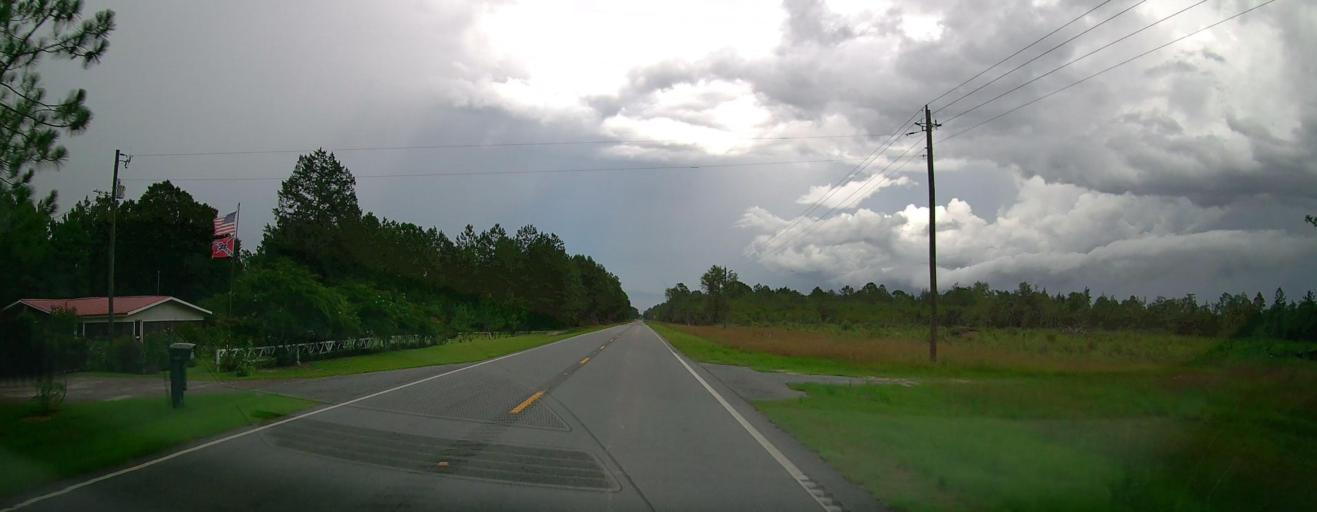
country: US
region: Georgia
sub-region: Pierce County
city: Blackshear
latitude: 31.3662
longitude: -82.0882
